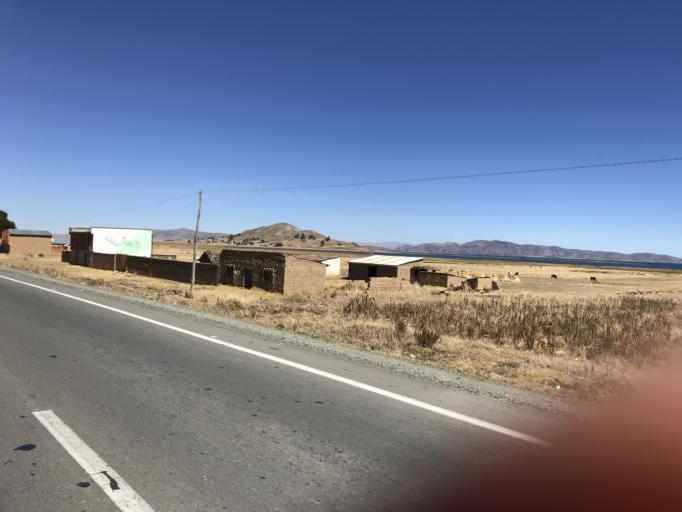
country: BO
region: La Paz
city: Huarina
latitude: -16.2083
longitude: -68.5936
